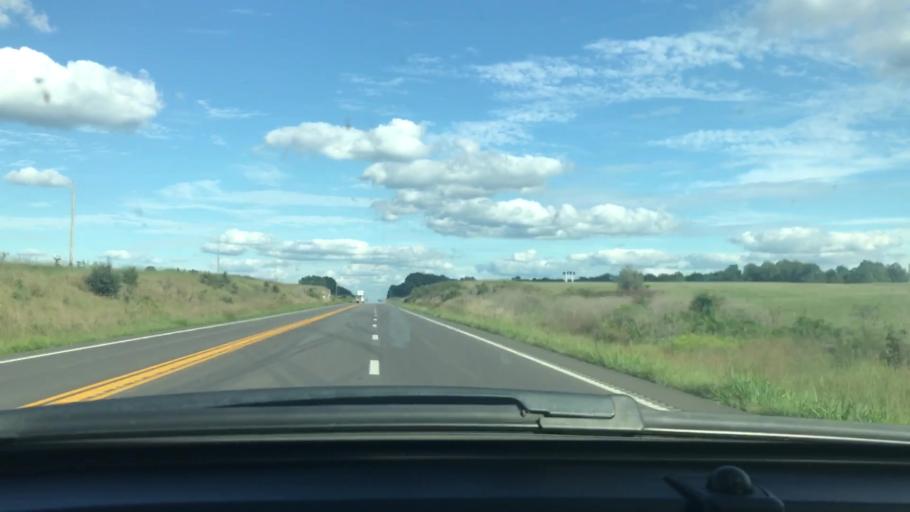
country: US
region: Missouri
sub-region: Oregon County
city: Thayer
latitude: 36.5853
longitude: -91.6218
